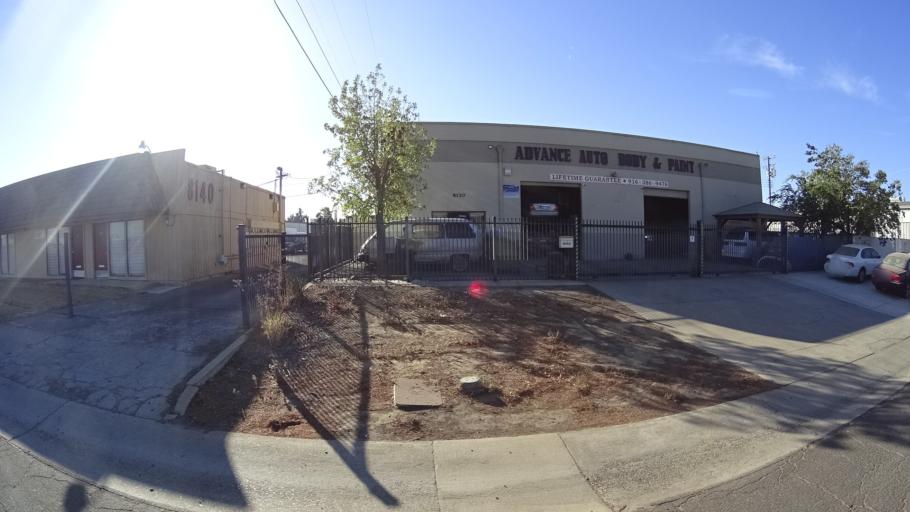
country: US
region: California
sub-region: Sacramento County
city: Florin
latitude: 38.5155
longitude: -121.4075
